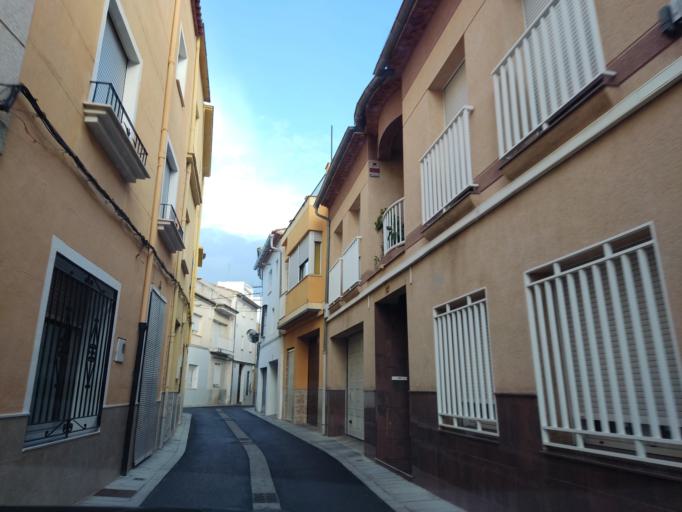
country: ES
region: Valencia
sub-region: Provincia de Alicante
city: Pego
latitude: 38.8394
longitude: -0.1182
